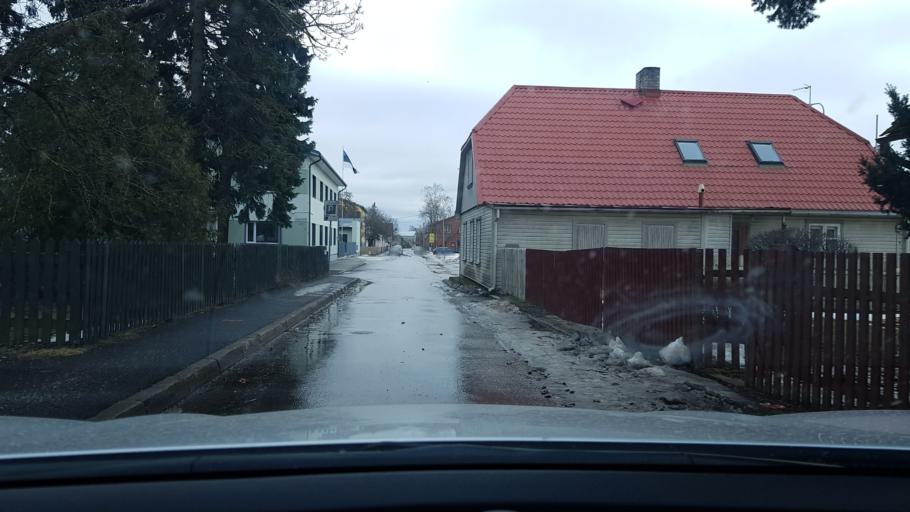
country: EE
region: Paernumaa
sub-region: Paernu linn
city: Parnu
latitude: 58.3803
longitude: 24.5099
